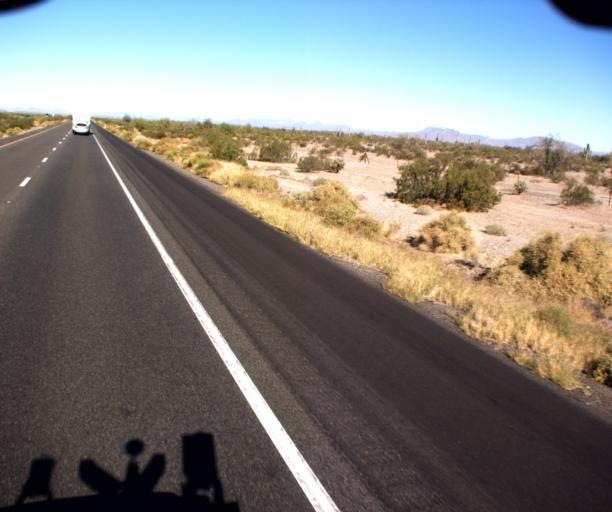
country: US
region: Arizona
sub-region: Maricopa County
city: Gila Bend
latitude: 32.9068
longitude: -112.5860
